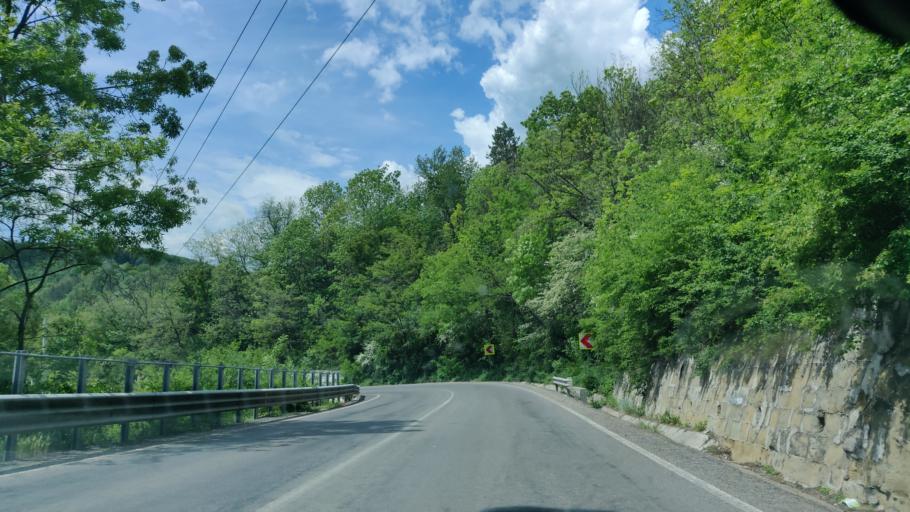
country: RO
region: Vrancea
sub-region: Comuna Vidra
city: Vidra
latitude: 45.8978
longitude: 26.8541
